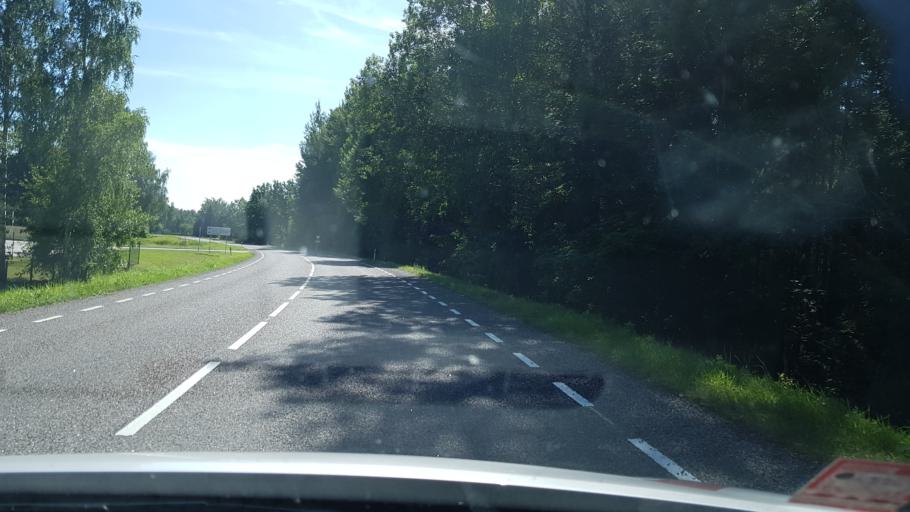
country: EE
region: Polvamaa
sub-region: Polva linn
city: Polva
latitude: 58.0554
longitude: 27.0417
